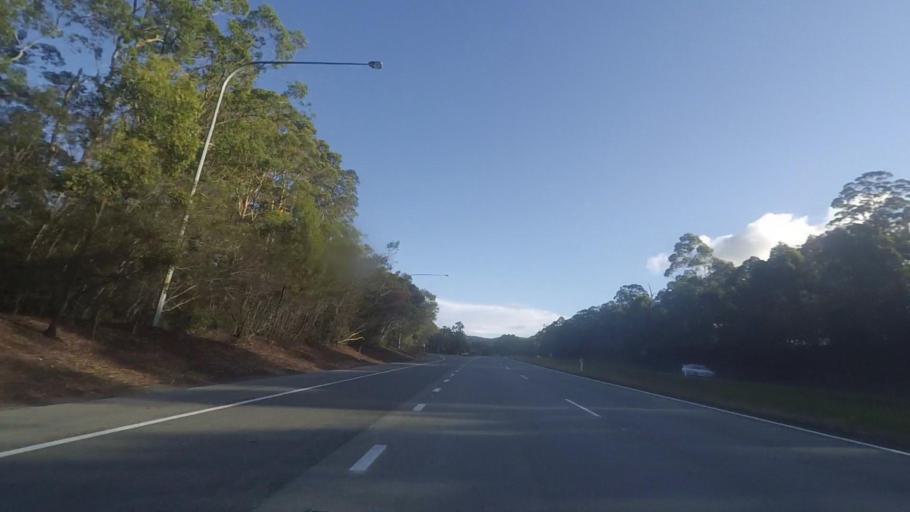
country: AU
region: New South Wales
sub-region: Great Lakes
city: Nabiac
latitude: -32.2498
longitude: 152.3231
